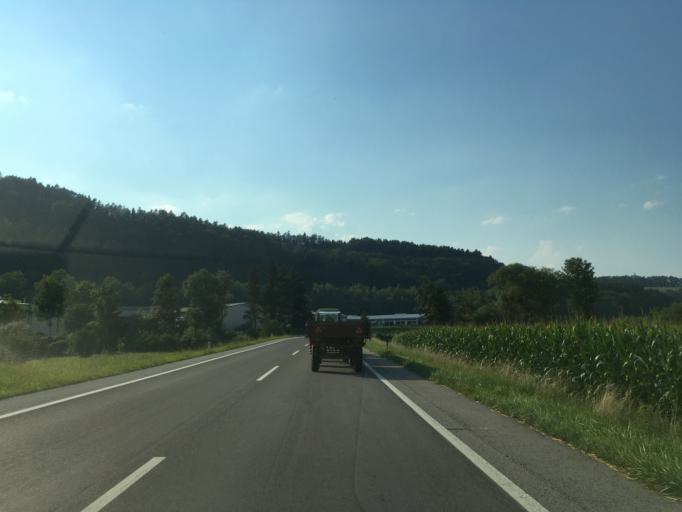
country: AT
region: Lower Austria
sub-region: Politischer Bezirk Neunkirchen
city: Warth
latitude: 47.6434
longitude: 16.1282
